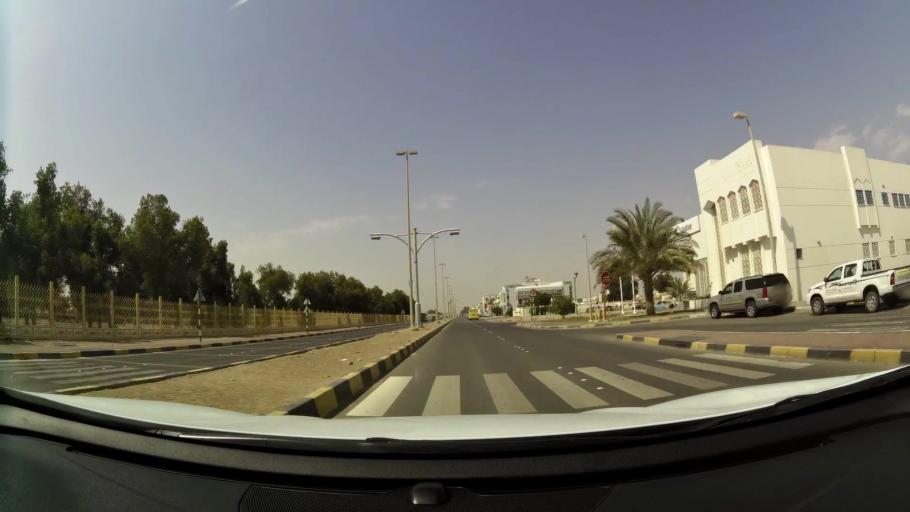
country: AE
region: Abu Dhabi
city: Abu Dhabi
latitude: 24.2851
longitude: 54.6437
